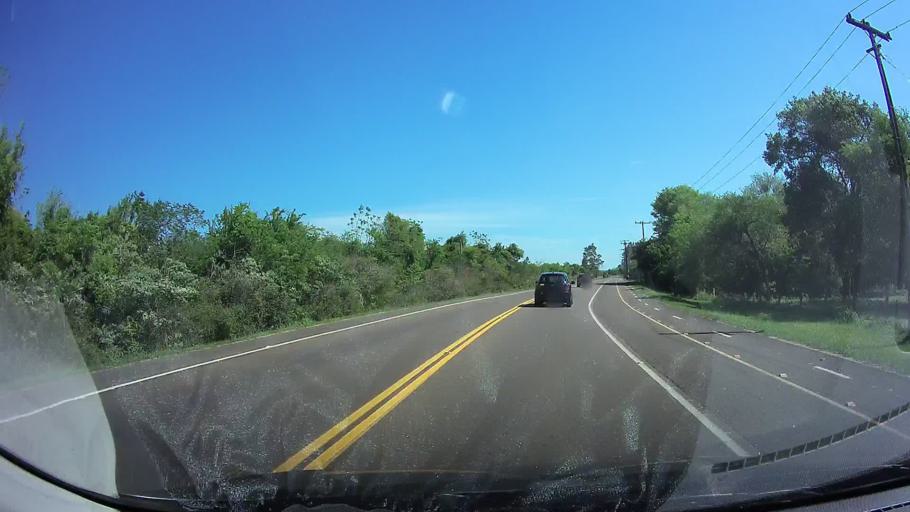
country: PY
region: Cordillera
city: San Bernardino
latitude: -25.2619
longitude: -57.3192
